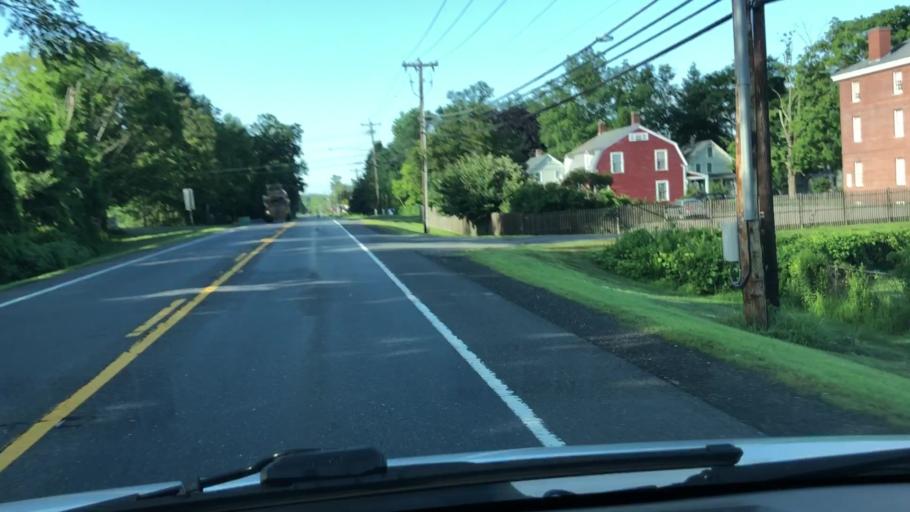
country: US
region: Massachusetts
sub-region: Franklin County
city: Greenfield
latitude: 42.5439
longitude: -72.6017
